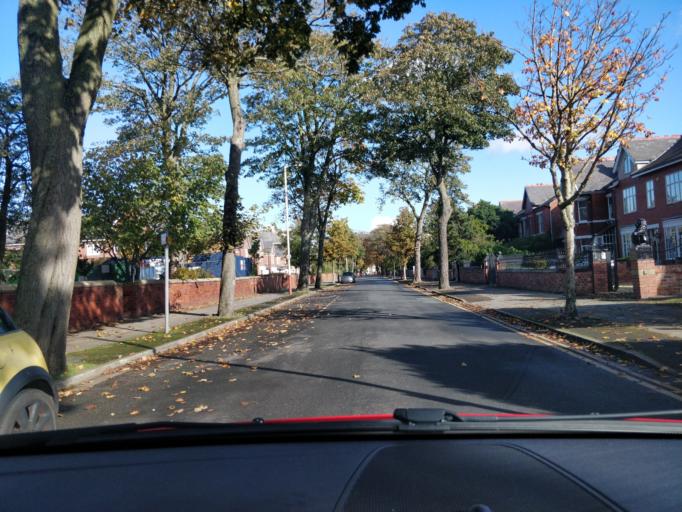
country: GB
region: England
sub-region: Sefton
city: Southport
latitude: 53.6382
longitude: -2.9856
